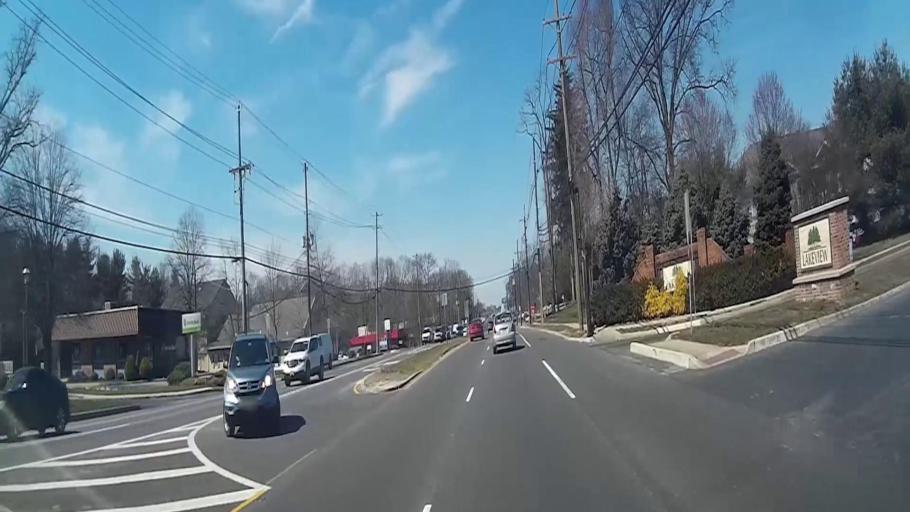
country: US
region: New Jersey
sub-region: Camden County
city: Greentree
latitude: 39.8998
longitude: -74.9580
